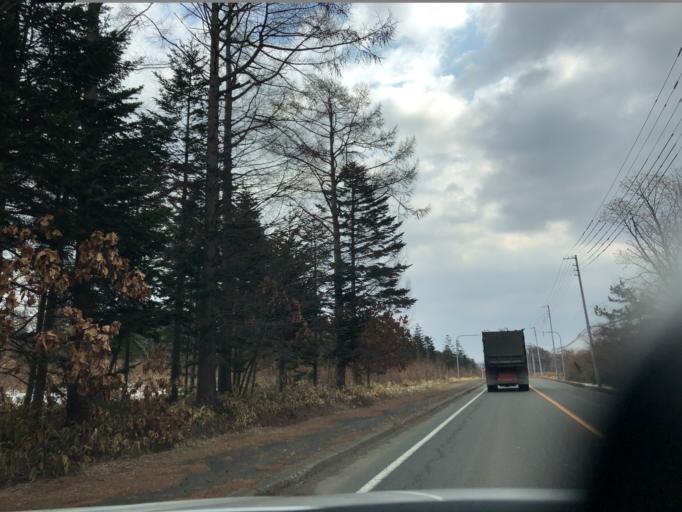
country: JP
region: Hokkaido
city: Chitose
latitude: 42.7593
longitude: 141.7877
